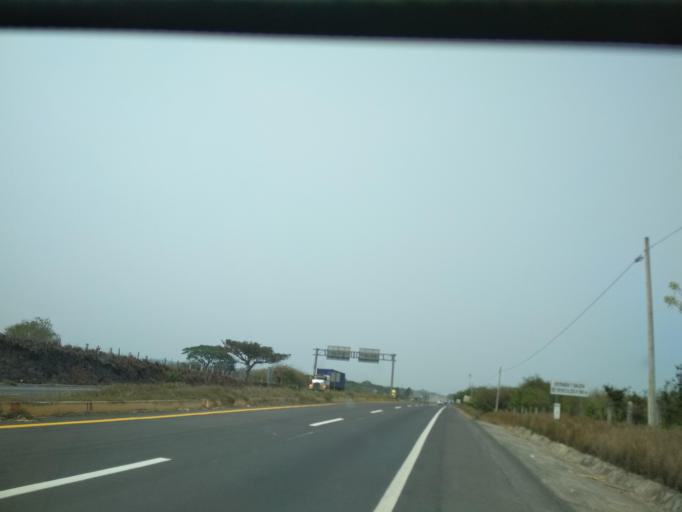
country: MX
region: Veracruz
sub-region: Veracruz
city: Delfino Victoria (Santa Fe)
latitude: 19.1972
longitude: -96.2735
